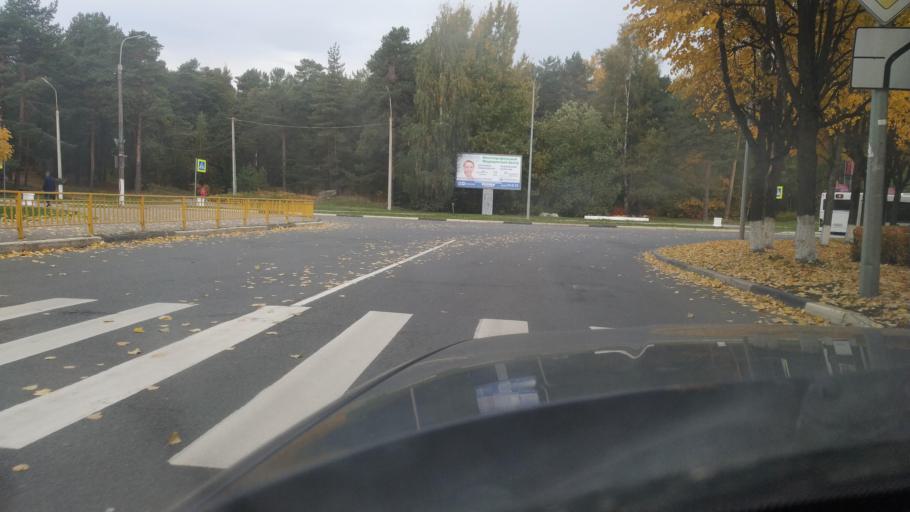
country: RU
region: Leningrad
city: Sosnovyy Bor
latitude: 59.8974
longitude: 29.0844
